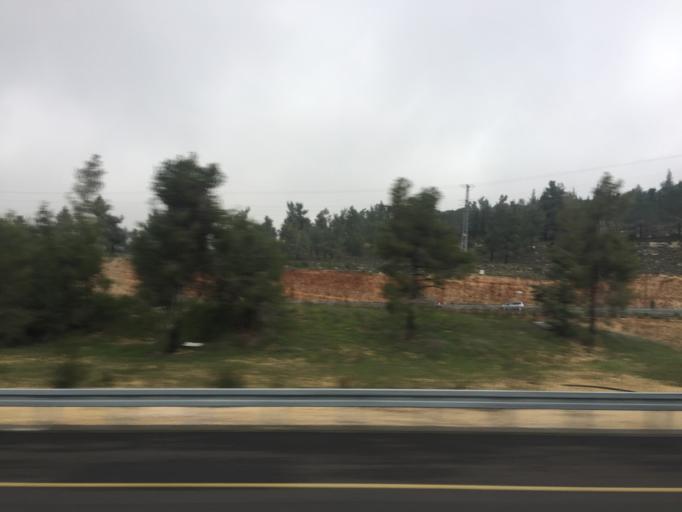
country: PS
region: West Bank
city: Bayt Surik
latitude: 31.7996
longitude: 35.1385
